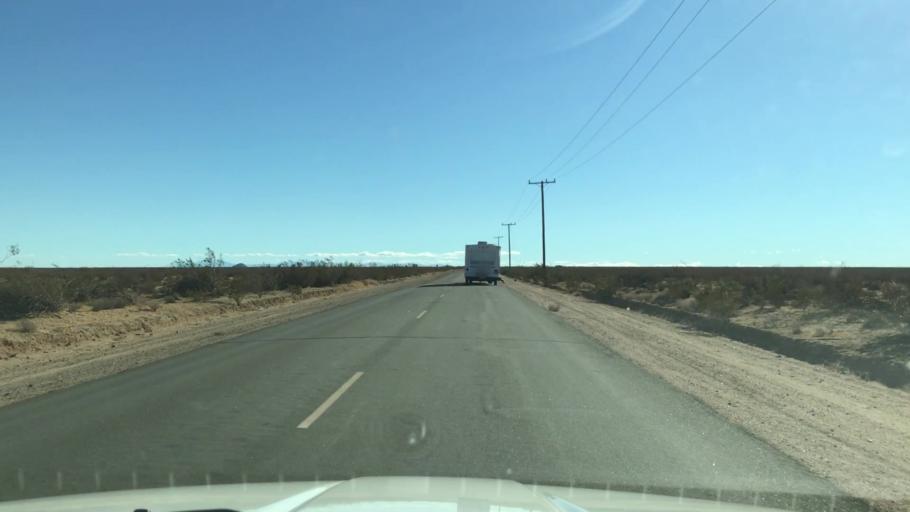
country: US
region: California
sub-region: Kern County
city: California City
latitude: 35.2294
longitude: -117.9859
